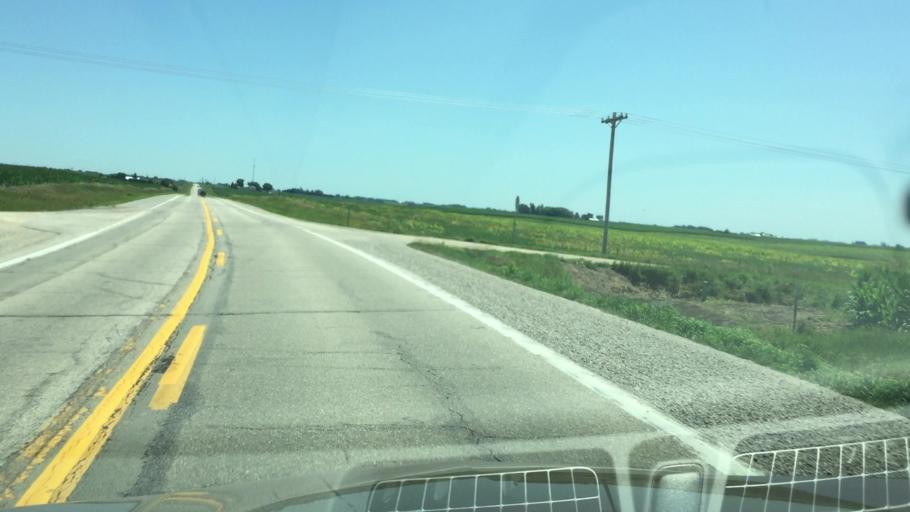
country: US
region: Iowa
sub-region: Cedar County
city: Mechanicsville
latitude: 41.8888
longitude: -91.2108
